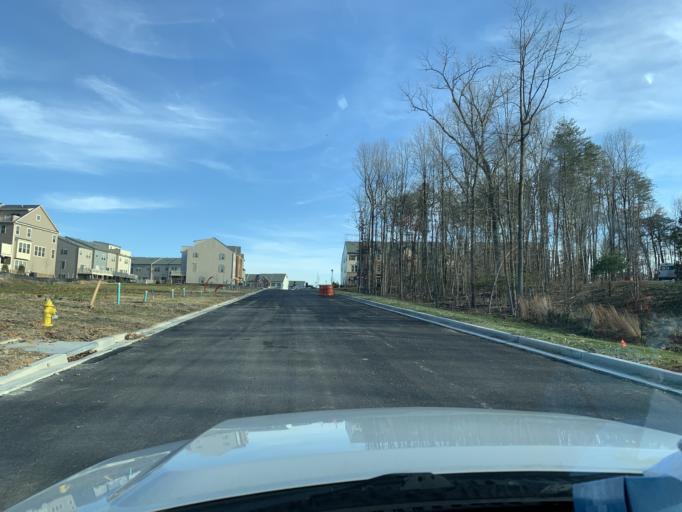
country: US
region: Maryland
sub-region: Anne Arundel County
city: Fort Meade
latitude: 39.1322
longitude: -76.7535
